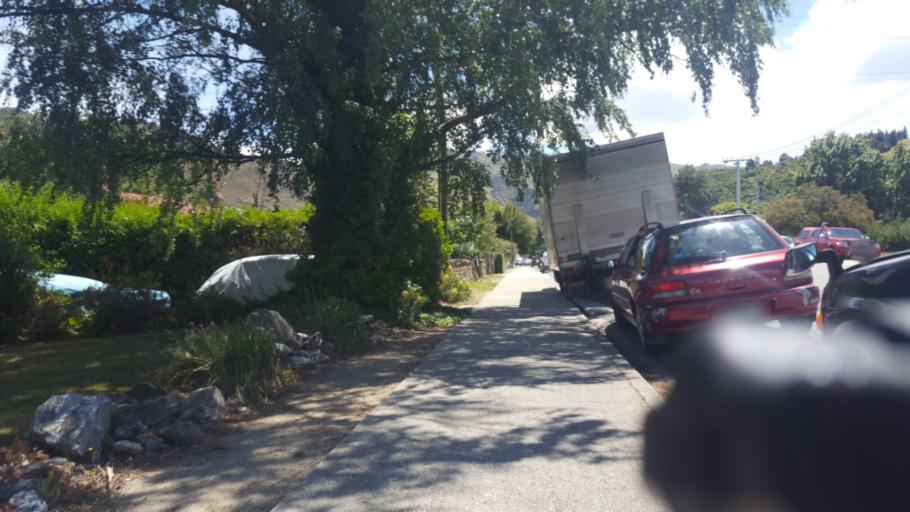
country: NZ
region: Otago
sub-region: Queenstown-Lakes District
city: Wanaka
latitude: -45.1881
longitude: 169.3181
